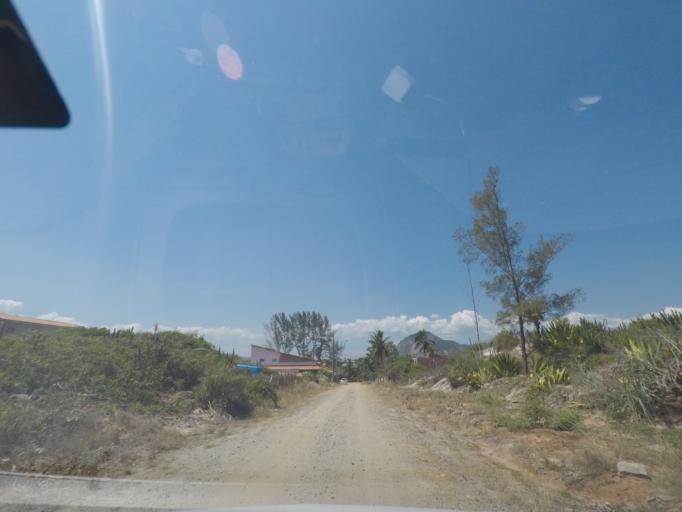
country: BR
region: Rio de Janeiro
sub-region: Marica
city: Marica
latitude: -22.9739
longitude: -42.9225
